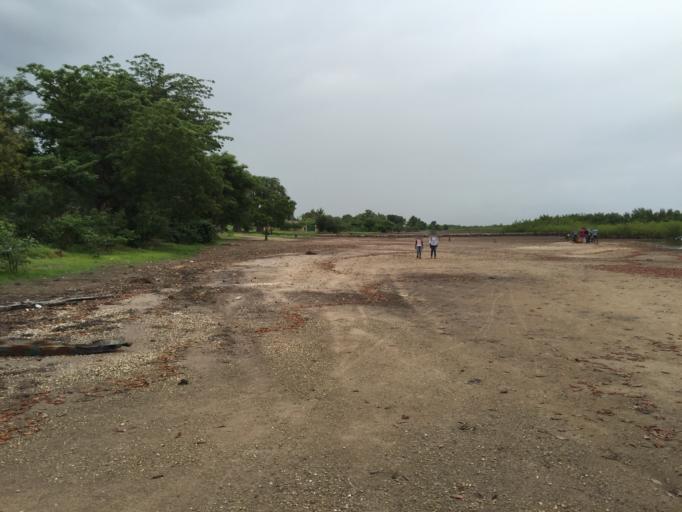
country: SN
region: Fatick
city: Sokone
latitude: 13.7862
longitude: -16.4787
